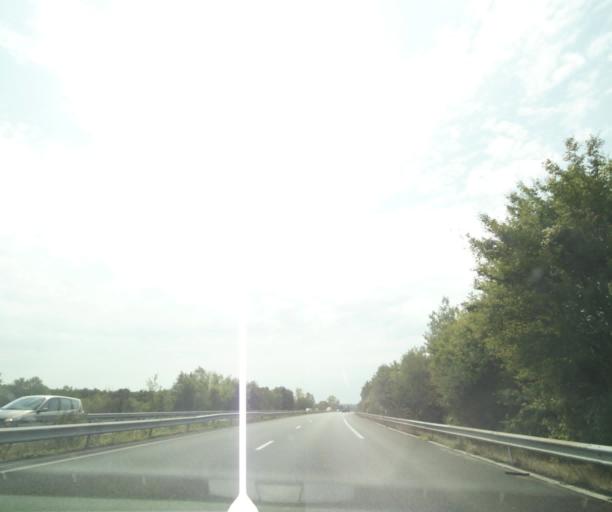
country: FR
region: Poitou-Charentes
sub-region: Departement de la Charente-Maritime
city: Bussac-sur-Charente
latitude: 45.8305
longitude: -0.6314
